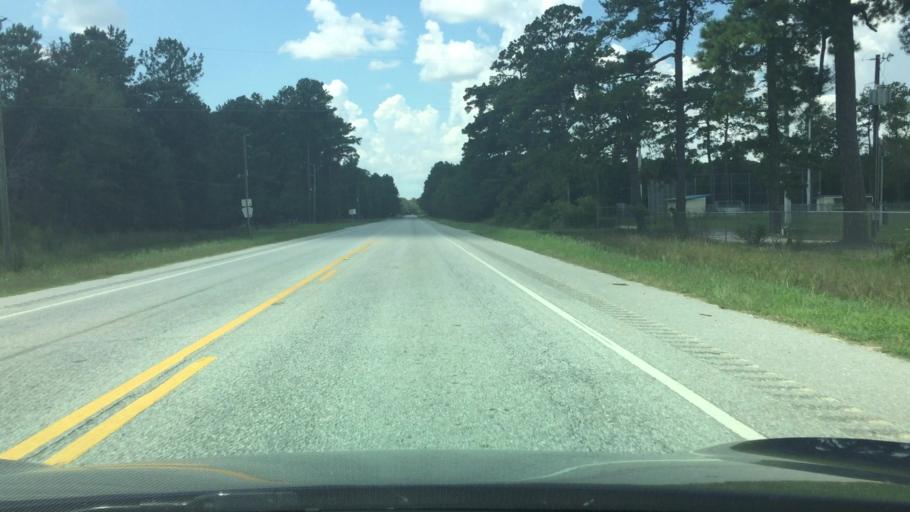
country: US
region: Alabama
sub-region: Montgomery County
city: Pike Road
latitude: 32.3819
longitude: -85.9904
